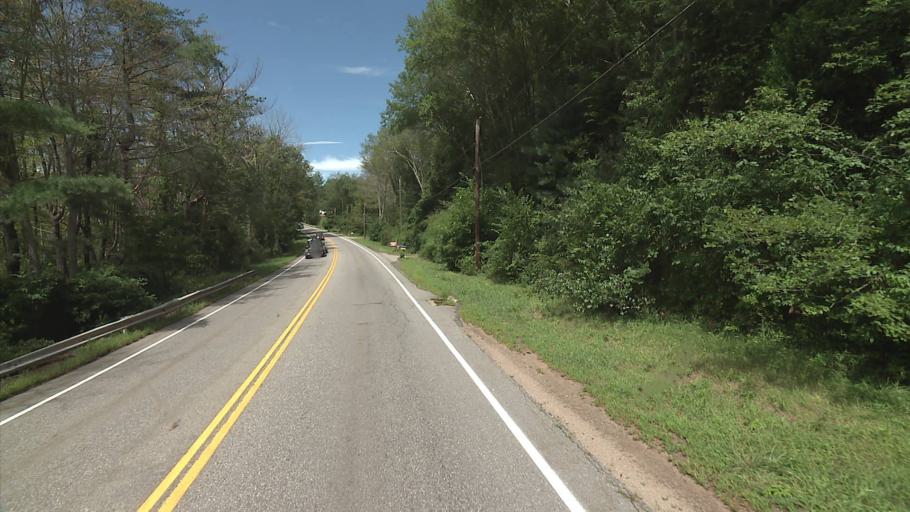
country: US
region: Connecticut
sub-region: Tolland County
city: Mansfield City
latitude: 41.7801
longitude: -72.2128
